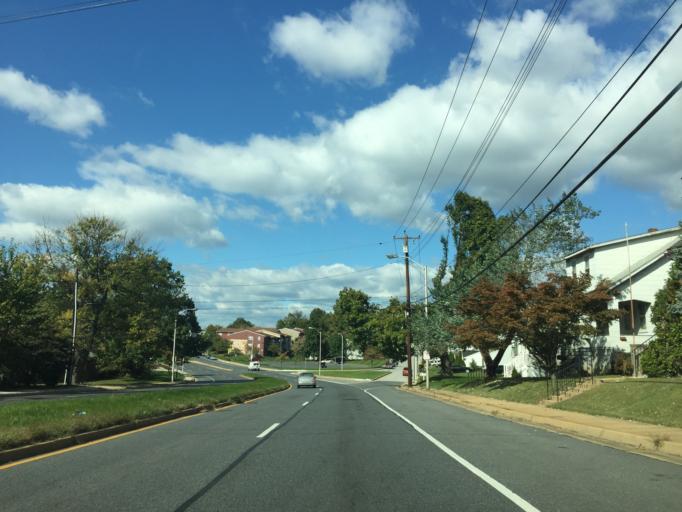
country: US
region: Maryland
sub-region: Baltimore County
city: Rosedale
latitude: 39.3274
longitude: -76.5543
